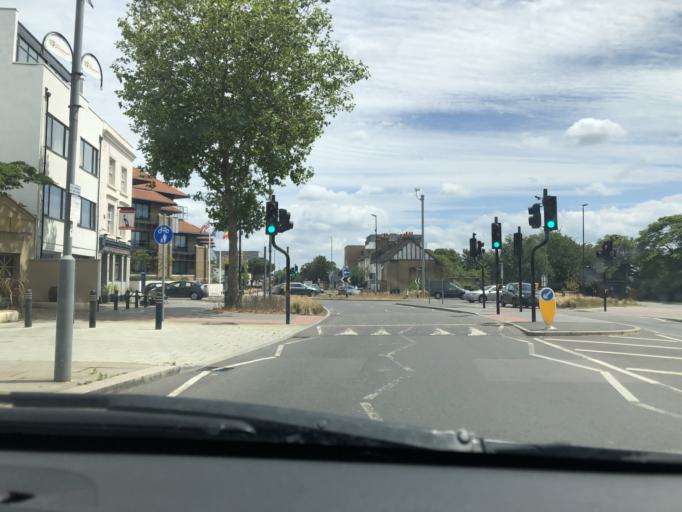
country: GB
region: England
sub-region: Greater London
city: Bexley
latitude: 51.4554
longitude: 0.1523
